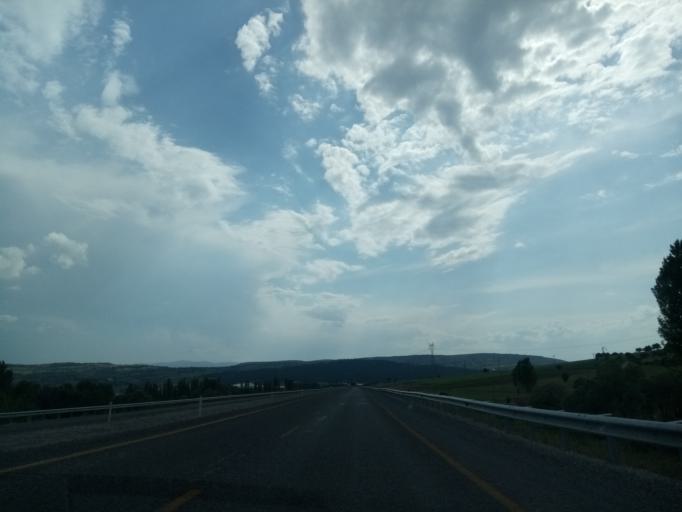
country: TR
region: Isparta
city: Bagkonak
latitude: 38.1998
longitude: 31.2546
